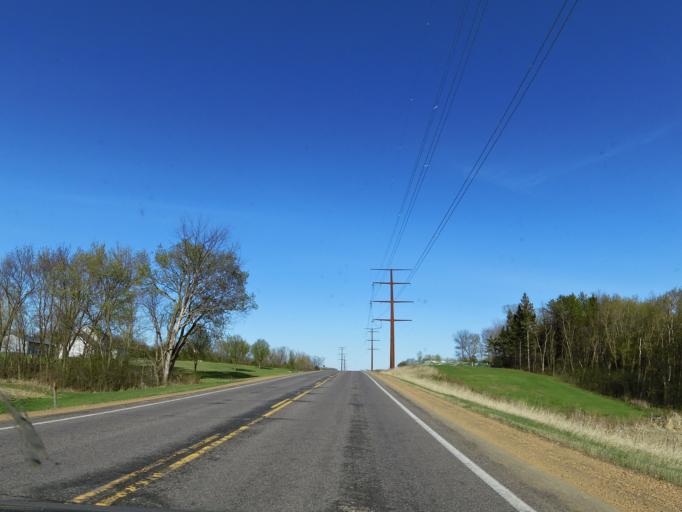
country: US
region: Minnesota
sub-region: Rice County
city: Lonsdale
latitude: 44.5722
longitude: -93.4713
